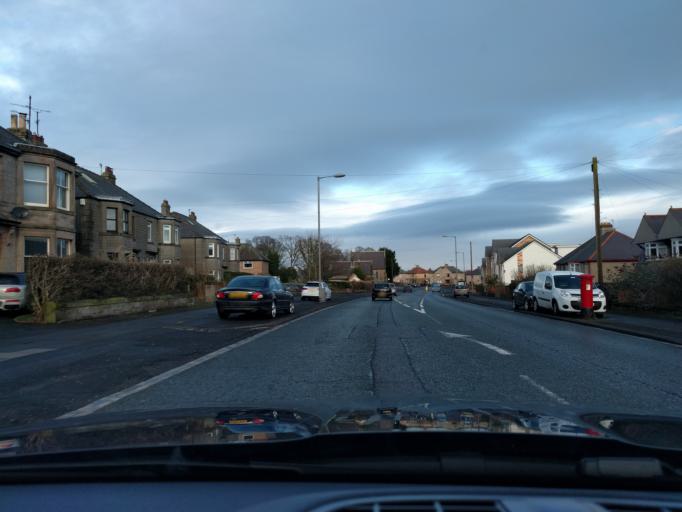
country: GB
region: England
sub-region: Northumberland
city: Berwick-Upon-Tweed
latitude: 55.7786
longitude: -2.0112
